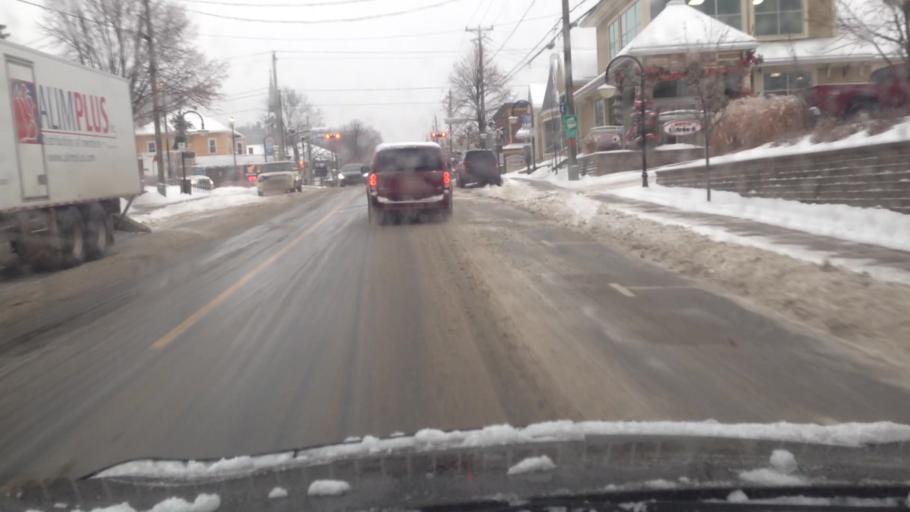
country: CA
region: Quebec
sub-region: Laurentides
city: Mont-Tremblant
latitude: 46.1184
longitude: -74.5974
